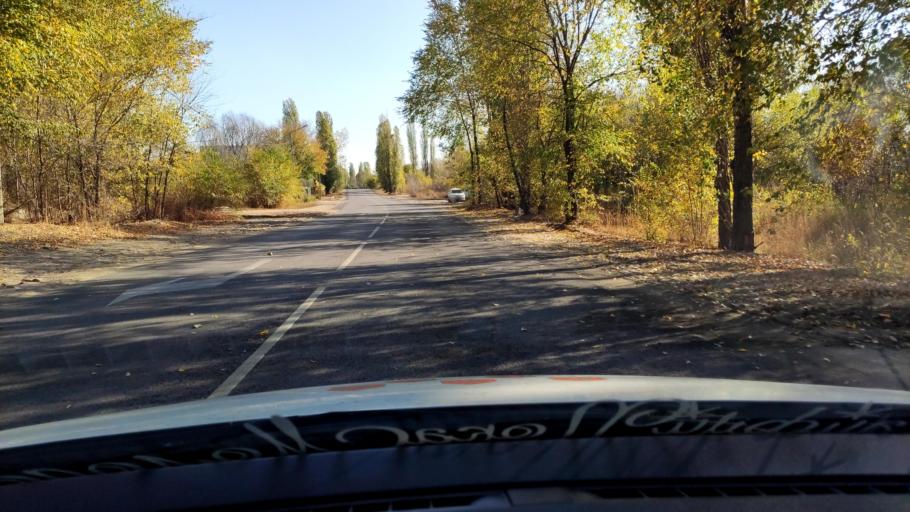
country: RU
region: Voronezj
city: Pridonskoy
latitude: 51.6856
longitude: 39.0631
